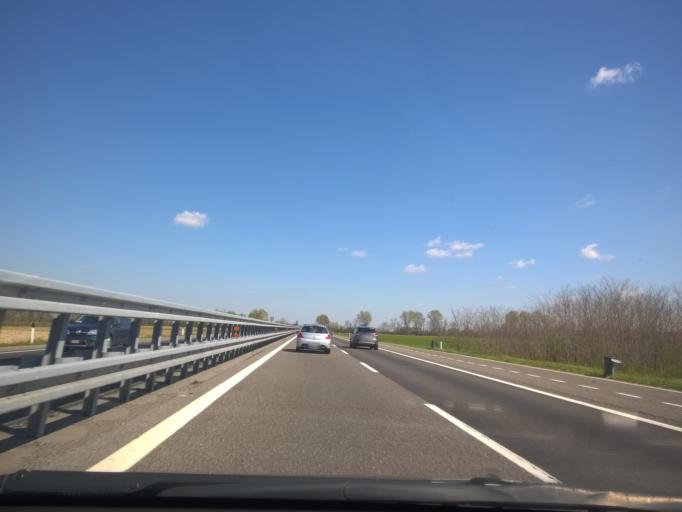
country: IT
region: Lombardy
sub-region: Provincia di Pavia
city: Arena Po
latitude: 45.0847
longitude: 9.3637
